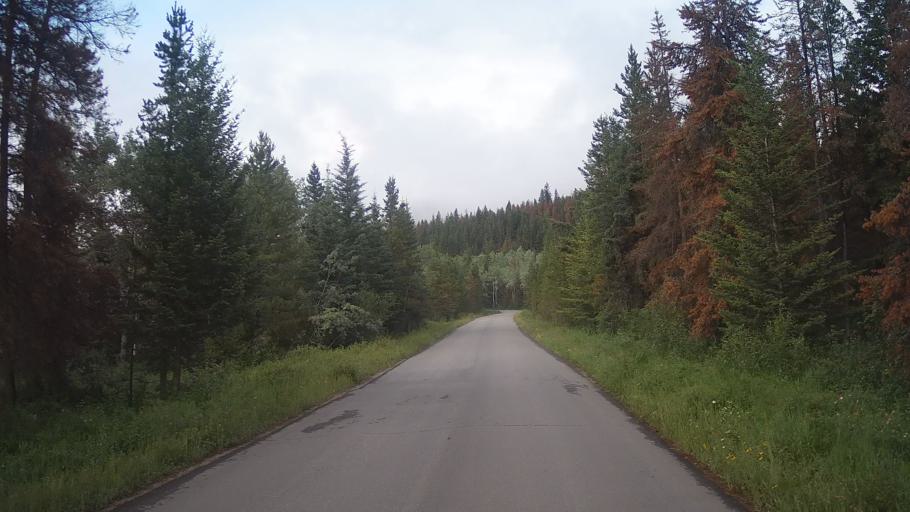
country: CA
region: Alberta
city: Jasper Park Lodge
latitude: 52.9674
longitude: -118.0596
